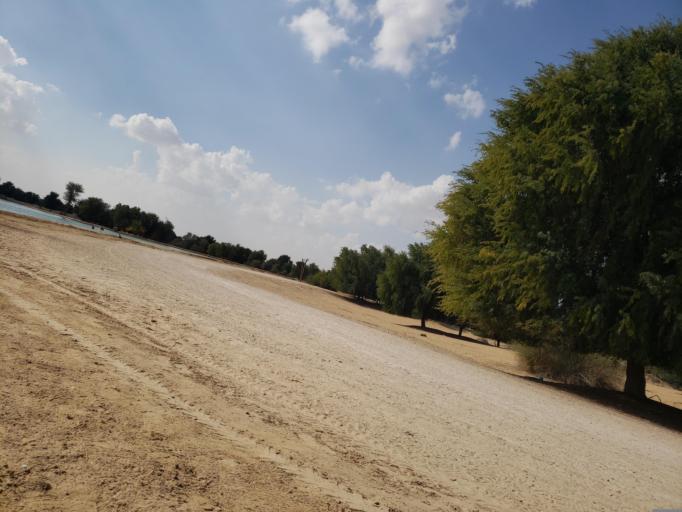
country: AE
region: Dubai
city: Dubai
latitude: 24.8332
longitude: 55.3797
